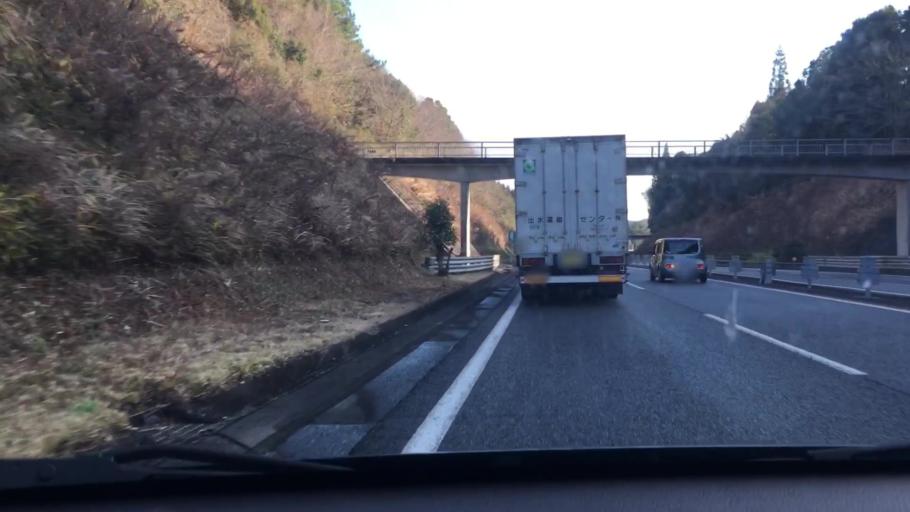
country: JP
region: Kagoshima
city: Okuchi-shinohara
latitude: 31.9109
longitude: 130.7053
